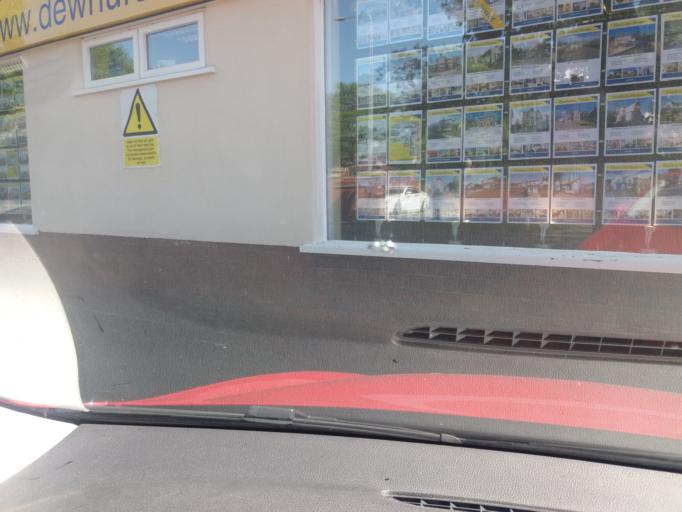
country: GB
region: England
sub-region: Lancashire
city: Preston
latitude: 53.7933
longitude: -2.7144
